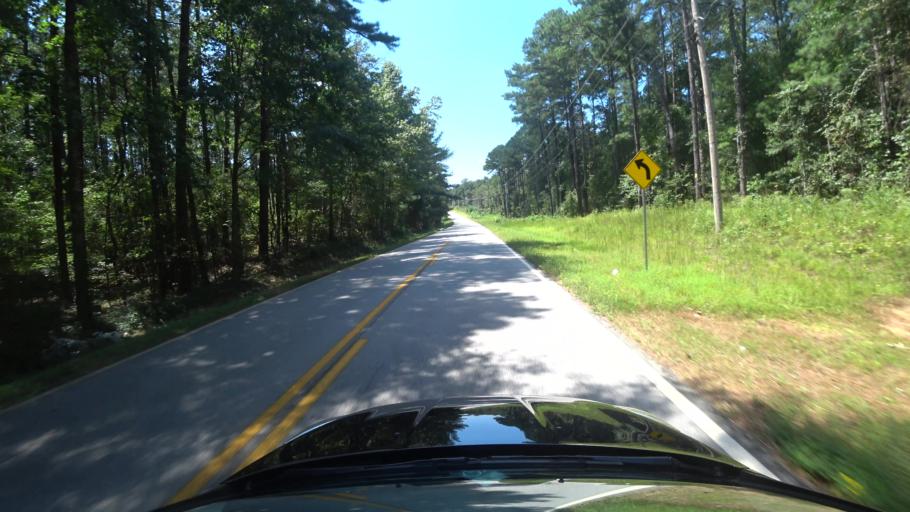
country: US
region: Georgia
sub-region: Newton County
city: Oxford
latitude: 33.6349
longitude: -83.8133
